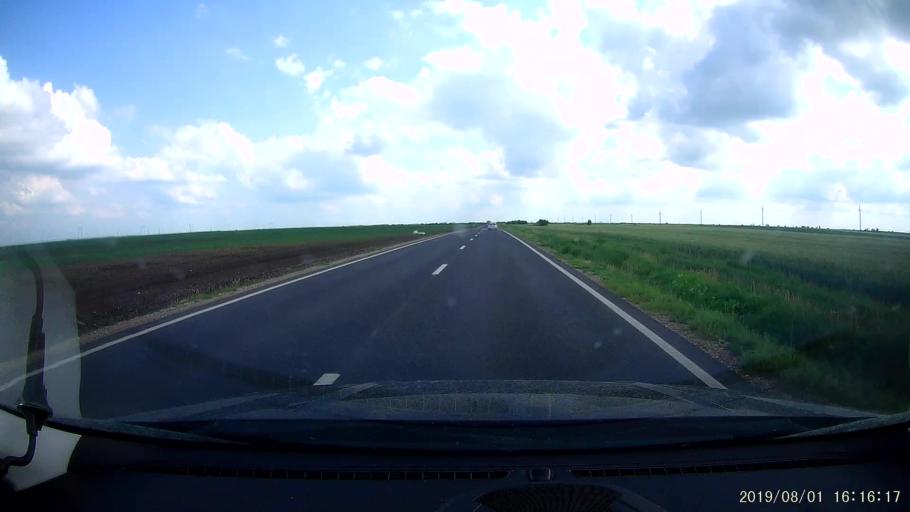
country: RO
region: Calarasi
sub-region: Comuna Stefan Voda
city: Stefan Voda
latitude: 44.3231
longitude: 27.3584
